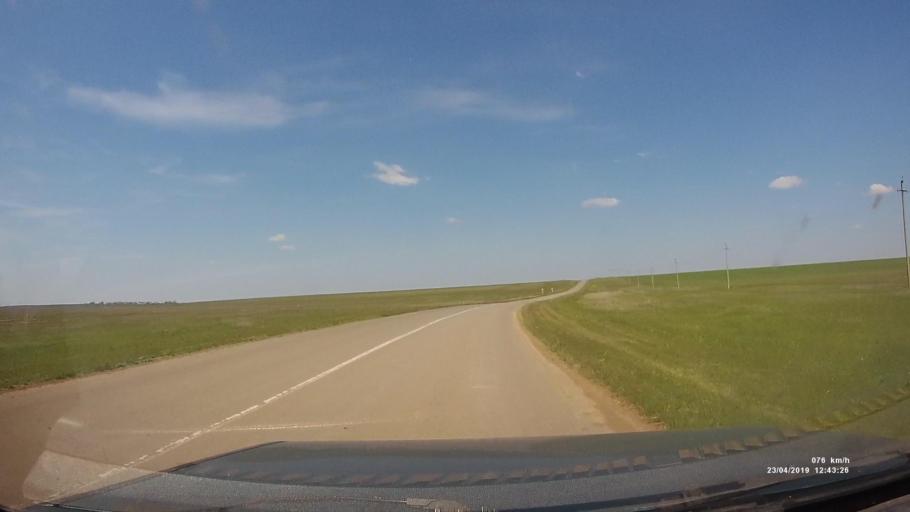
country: RU
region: Kalmykiya
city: Yashalta
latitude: 46.4642
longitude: 42.6505
